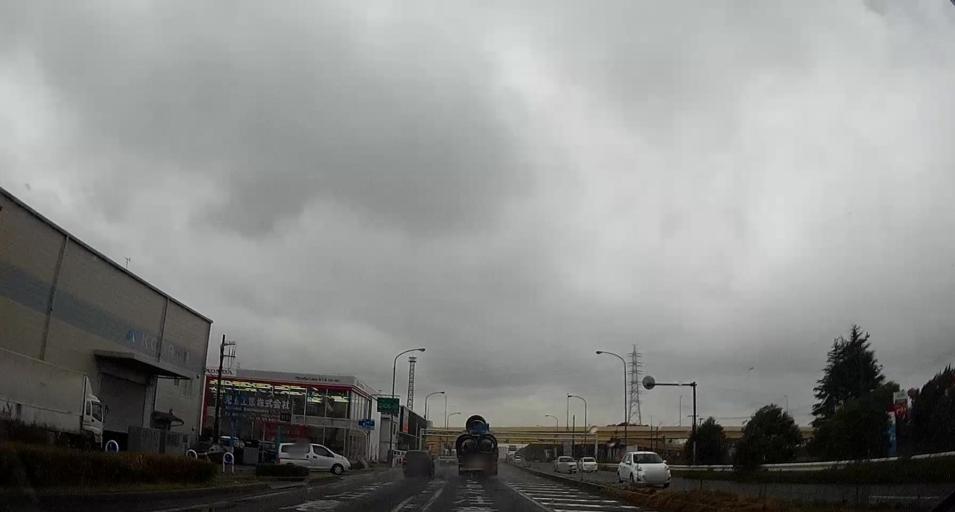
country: JP
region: Chiba
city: Ichihara
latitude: 35.5372
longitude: 140.1118
